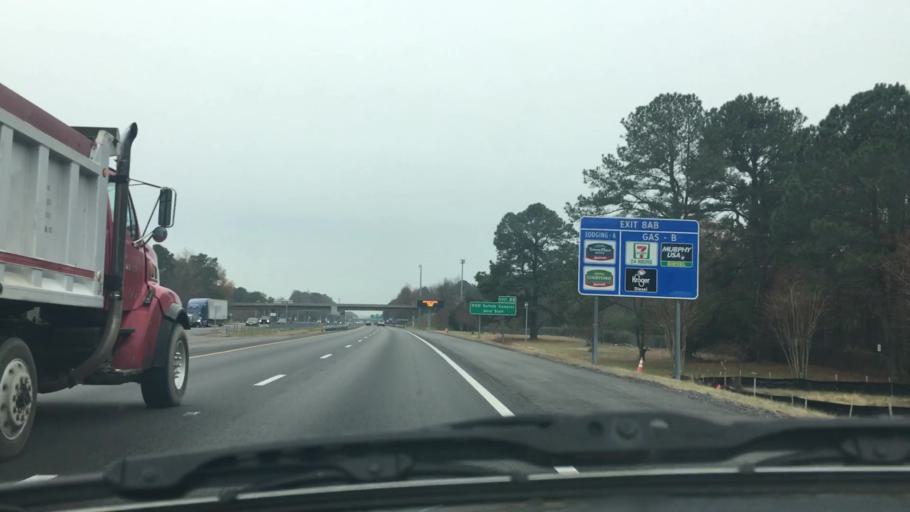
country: US
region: Virginia
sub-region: City of Newport News
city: Newport News
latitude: 36.8999
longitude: -76.4244
